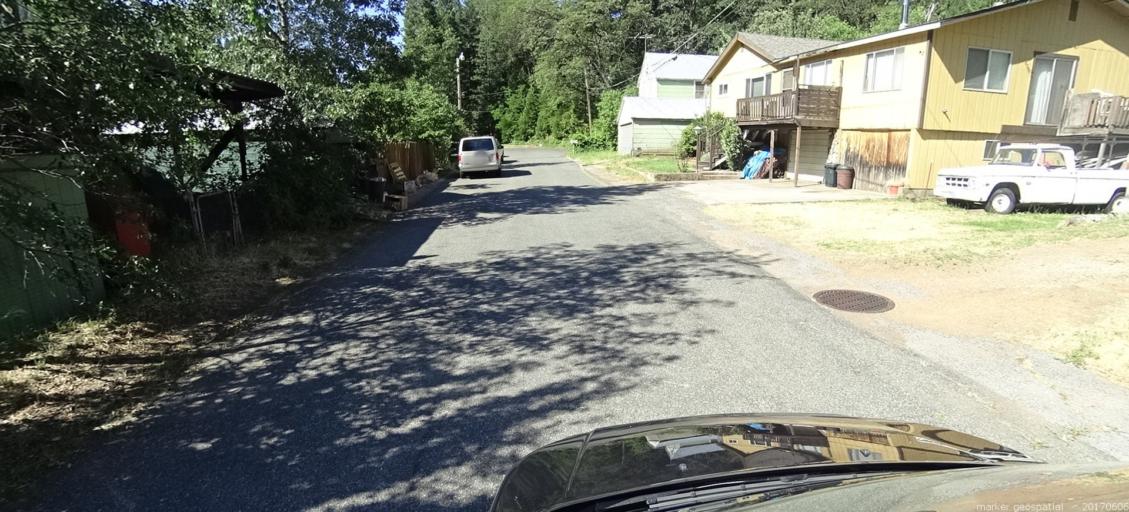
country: US
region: California
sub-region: Siskiyou County
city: Dunsmuir
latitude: 41.1997
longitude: -122.2753
